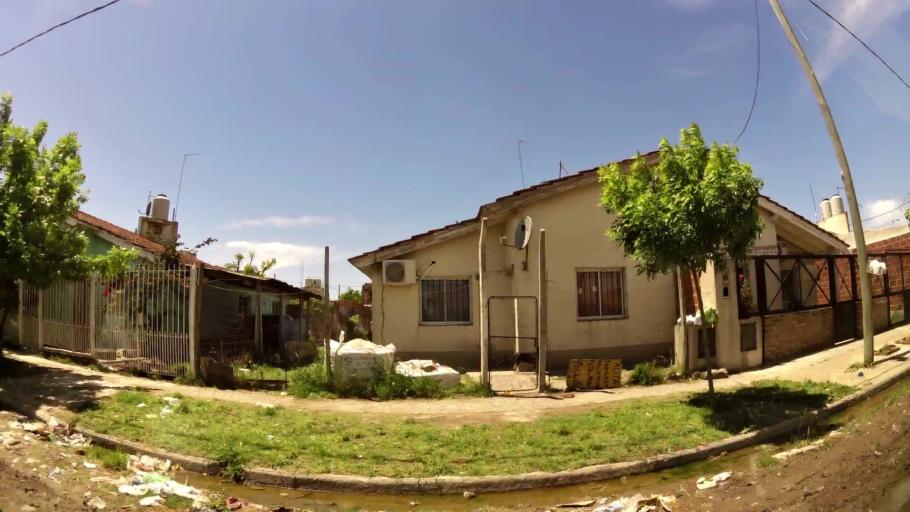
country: AR
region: Buenos Aires
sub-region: Partido de Quilmes
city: Quilmes
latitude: -34.7450
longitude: -58.3087
